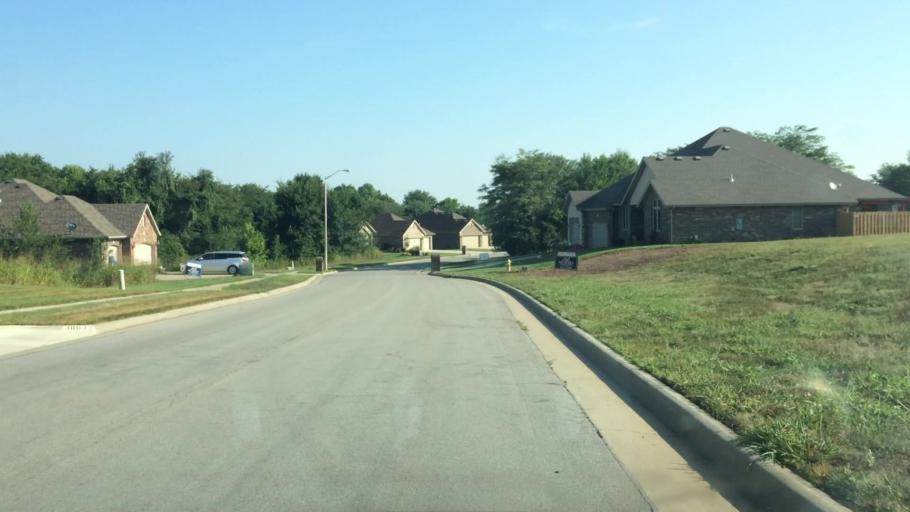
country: US
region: Missouri
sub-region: Greene County
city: Springfield
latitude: 37.2672
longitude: -93.2766
